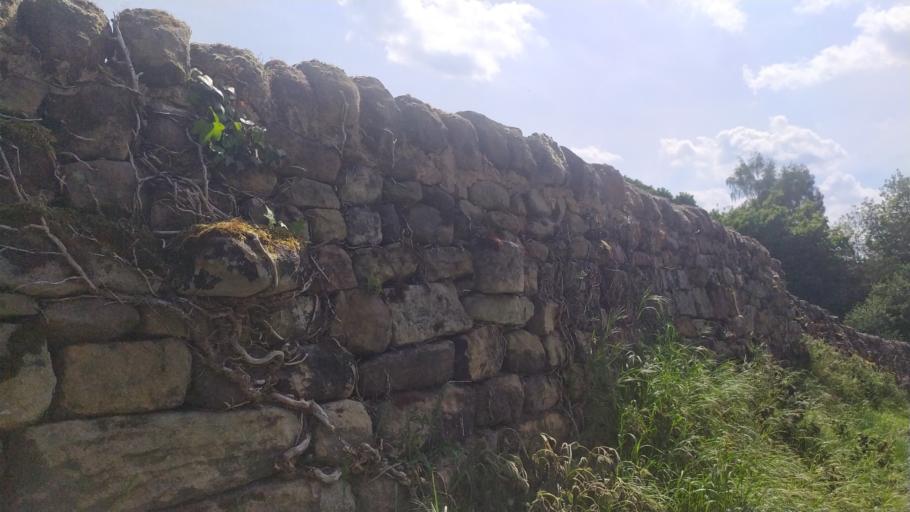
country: GB
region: England
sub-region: City and Borough of Leeds
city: Chapel Allerton
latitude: 53.8764
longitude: -1.5603
